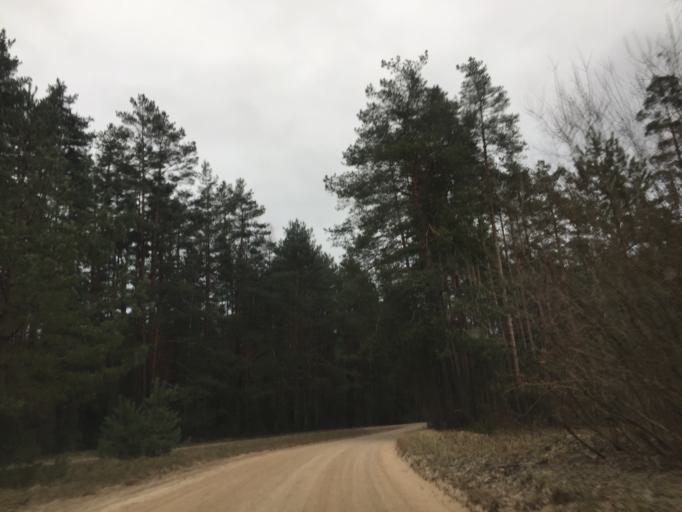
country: LV
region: Cesu Rajons
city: Cesis
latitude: 57.3523
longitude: 25.2582
